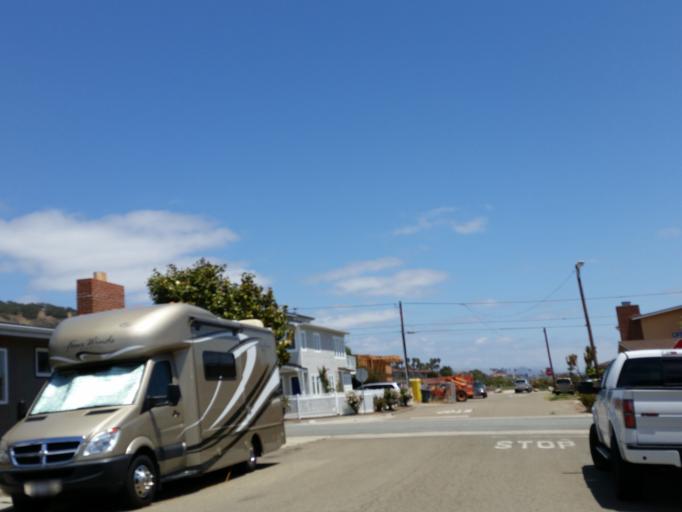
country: US
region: California
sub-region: San Luis Obispo County
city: Pismo Beach
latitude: 35.1544
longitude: -120.6676
